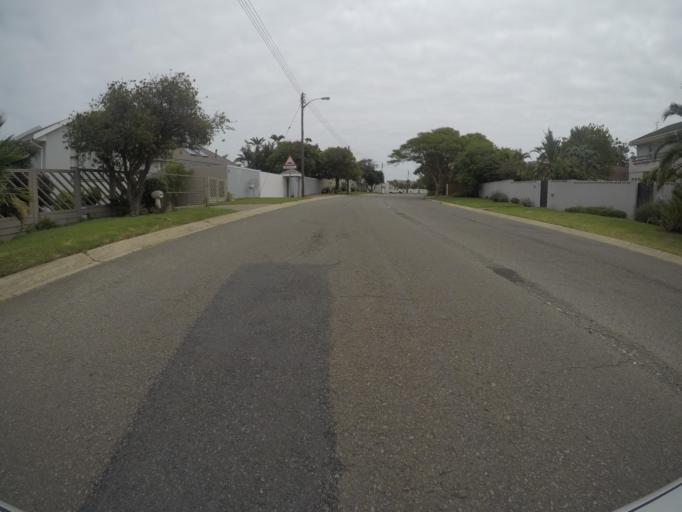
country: ZA
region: Eastern Cape
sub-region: Buffalo City Metropolitan Municipality
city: East London
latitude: -32.9790
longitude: 27.9495
